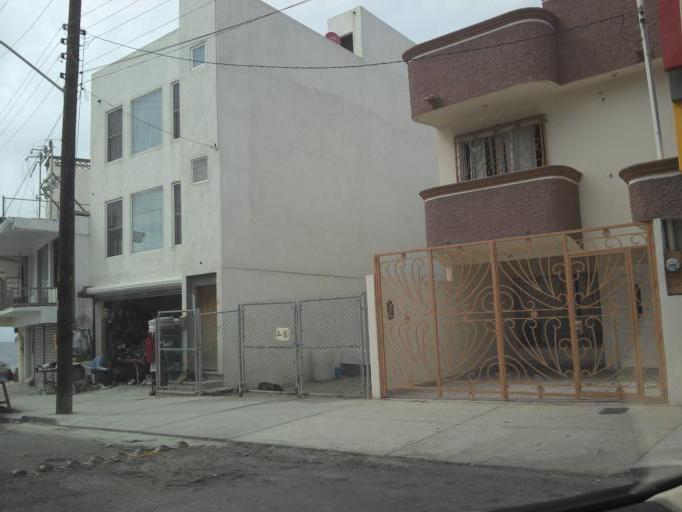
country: US
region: California
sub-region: San Diego County
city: Imperial Beach
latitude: 32.5231
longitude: -117.1233
